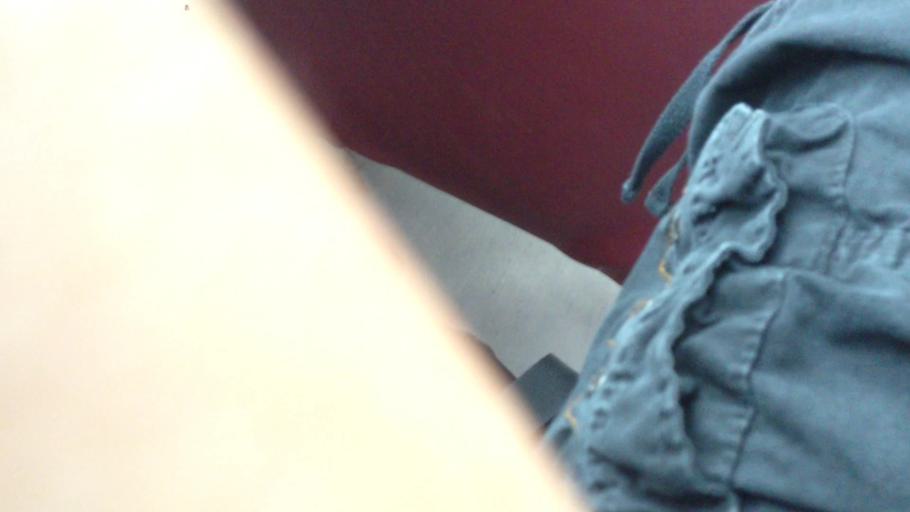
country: US
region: New York
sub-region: Ulster County
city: Lake Katrine
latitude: 41.9751
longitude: -73.9383
